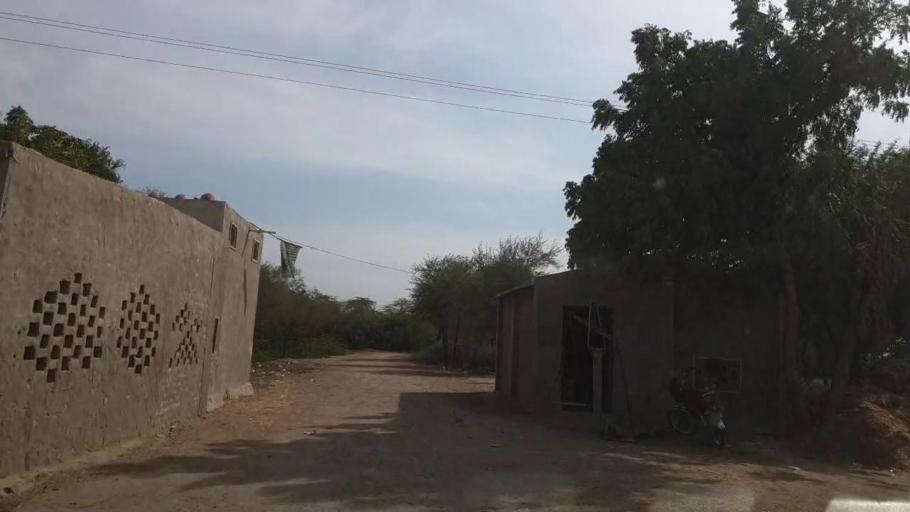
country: PK
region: Sindh
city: Nabisar
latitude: 25.0467
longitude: 69.5709
